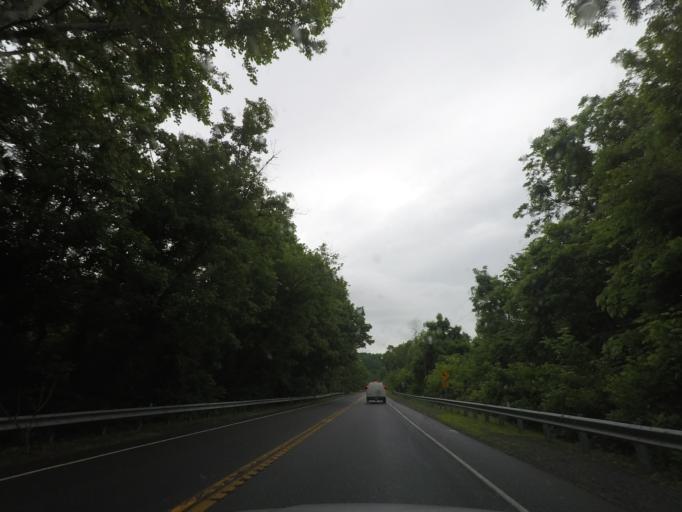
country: US
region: Virginia
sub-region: Loudoun County
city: Brambleton
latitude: 39.0283
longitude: -77.6220
